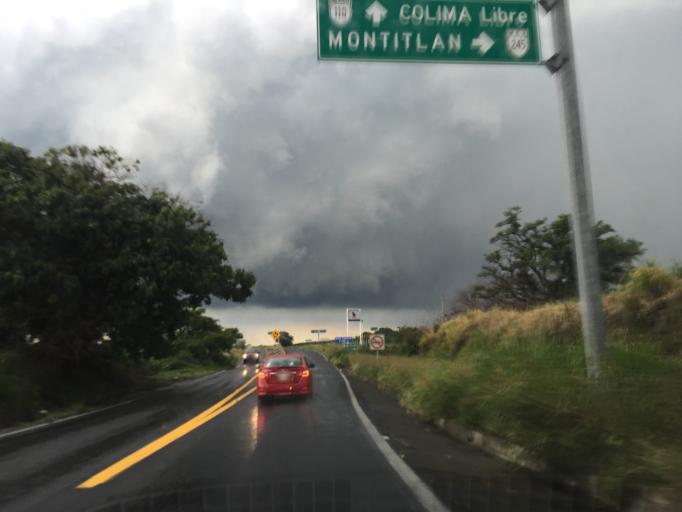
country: MX
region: Colima
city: Queseria
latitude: 19.3748
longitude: -103.5773
